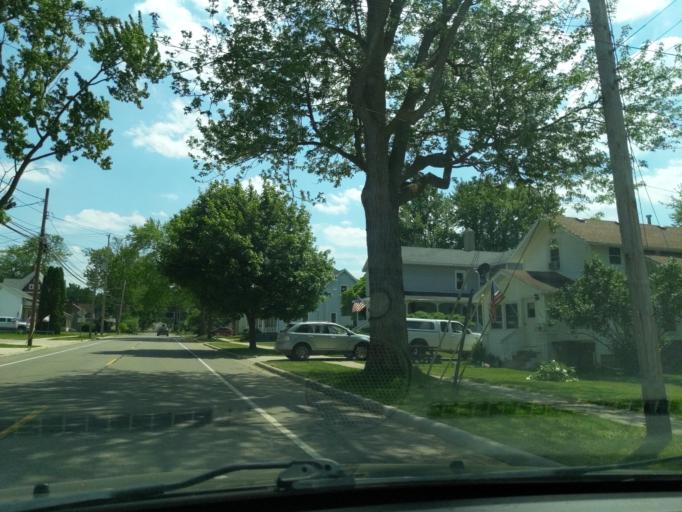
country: US
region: Michigan
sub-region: Clinton County
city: Saint Johns
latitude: 43.0044
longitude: -84.5626
